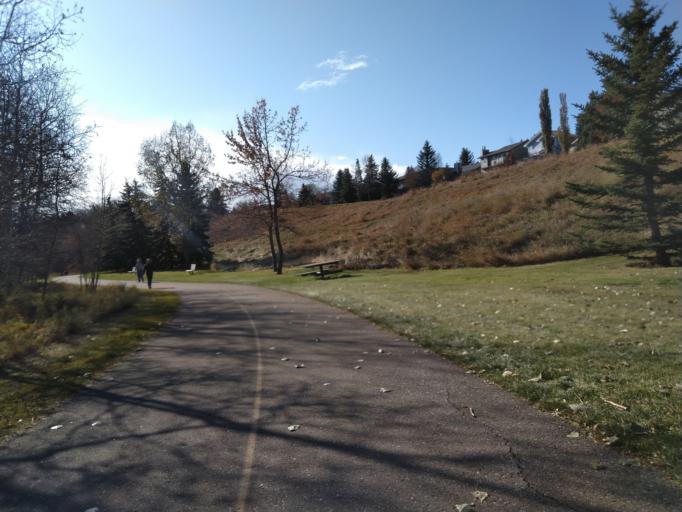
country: CA
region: Alberta
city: Calgary
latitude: 51.1344
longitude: -114.1515
